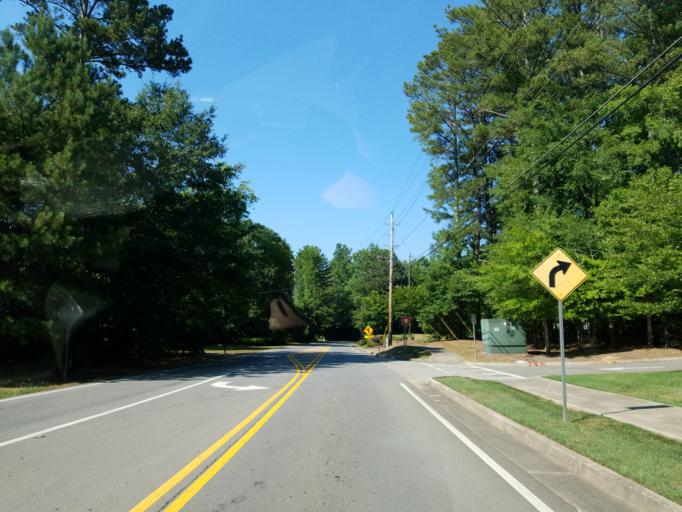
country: US
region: Georgia
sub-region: Fulton County
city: Milton
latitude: 34.1676
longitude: -84.3325
